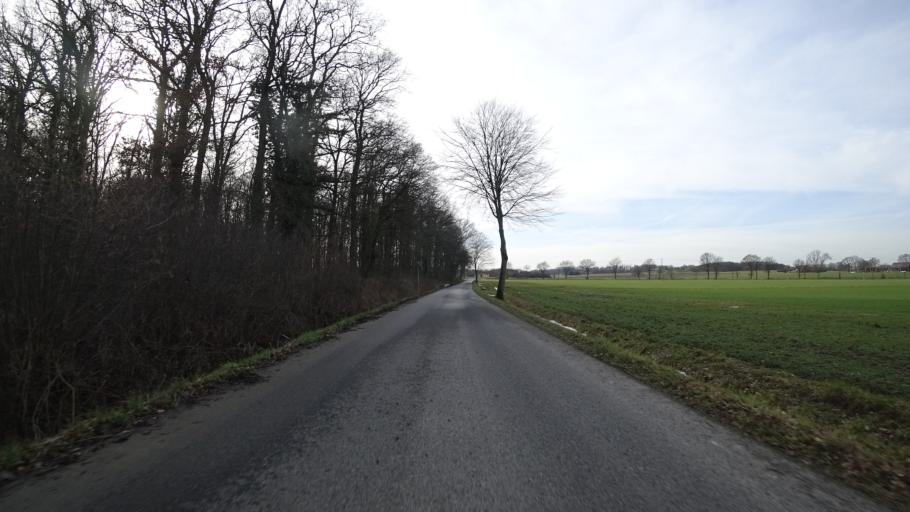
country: DE
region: North Rhine-Westphalia
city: Oelde
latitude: 51.8104
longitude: 8.1058
